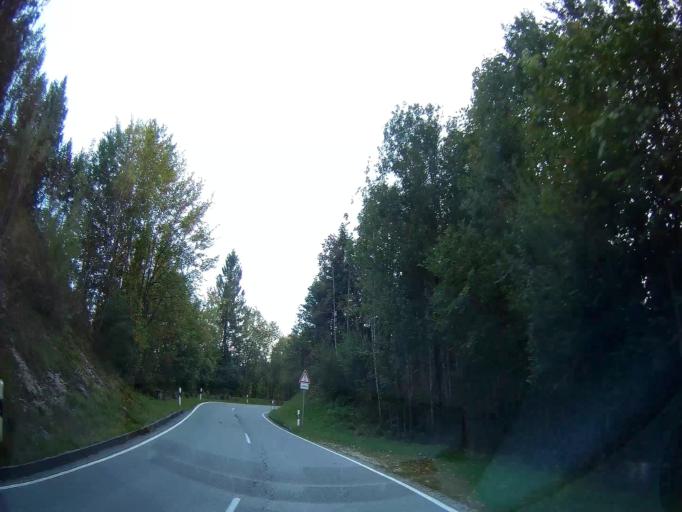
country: DE
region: Bavaria
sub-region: Upper Bavaria
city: Bischofswiesen
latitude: 47.6533
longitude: 12.9550
